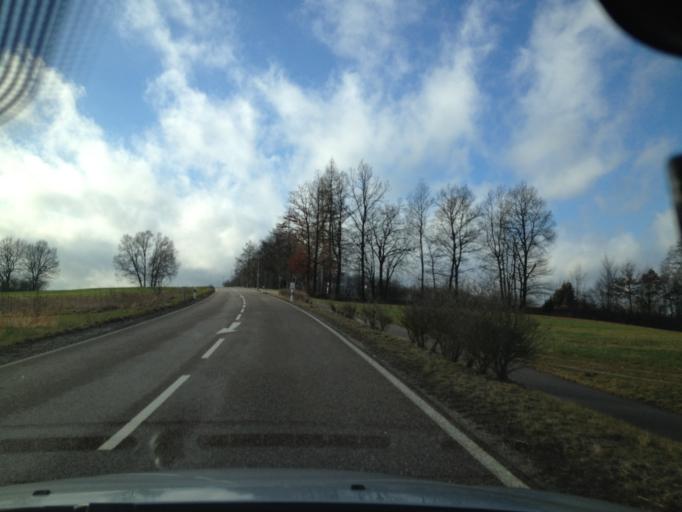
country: DE
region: Bavaria
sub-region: Swabia
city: Grossaitingen
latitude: 48.2615
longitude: 10.7440
